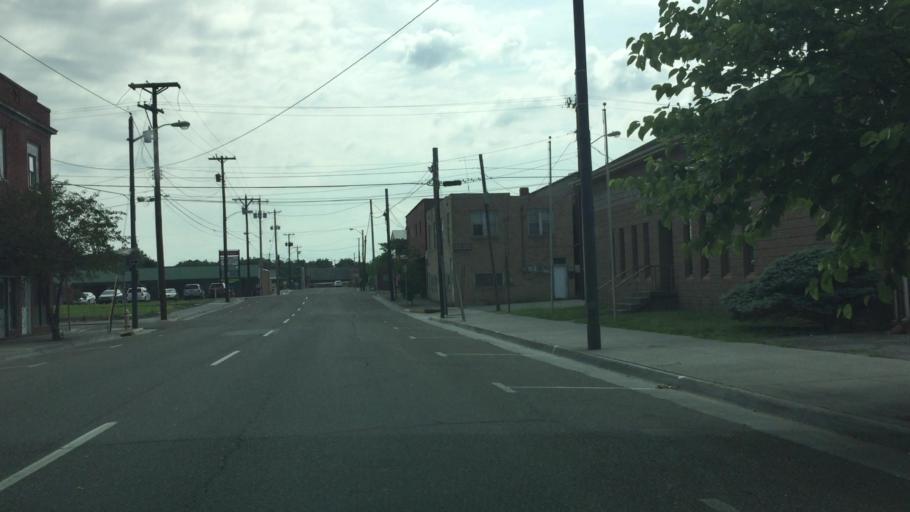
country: US
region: Virginia
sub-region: Pulaski County
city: Pulaski
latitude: 37.0477
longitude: -80.7780
